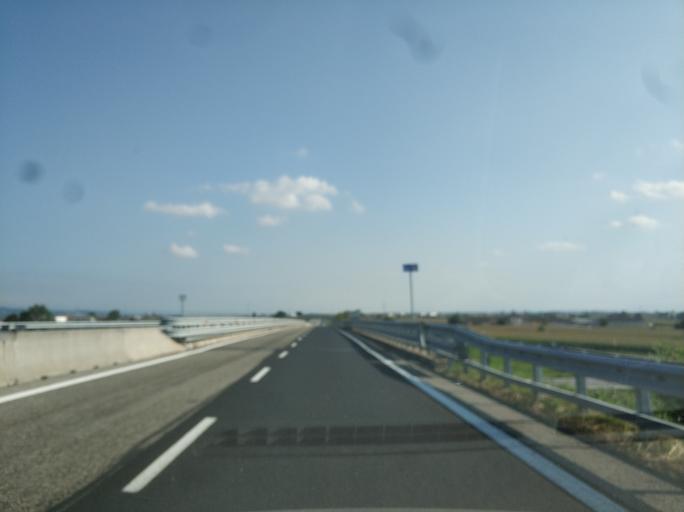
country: IT
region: Piedmont
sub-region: Provincia di Cuneo
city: Roreto
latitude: 44.6918
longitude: 7.8263
